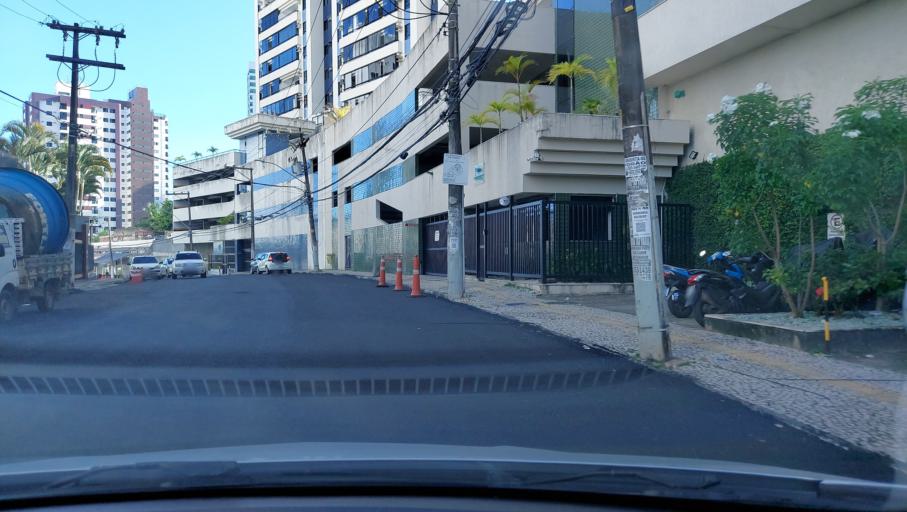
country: BR
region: Bahia
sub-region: Salvador
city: Salvador
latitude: -12.9865
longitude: -38.4540
